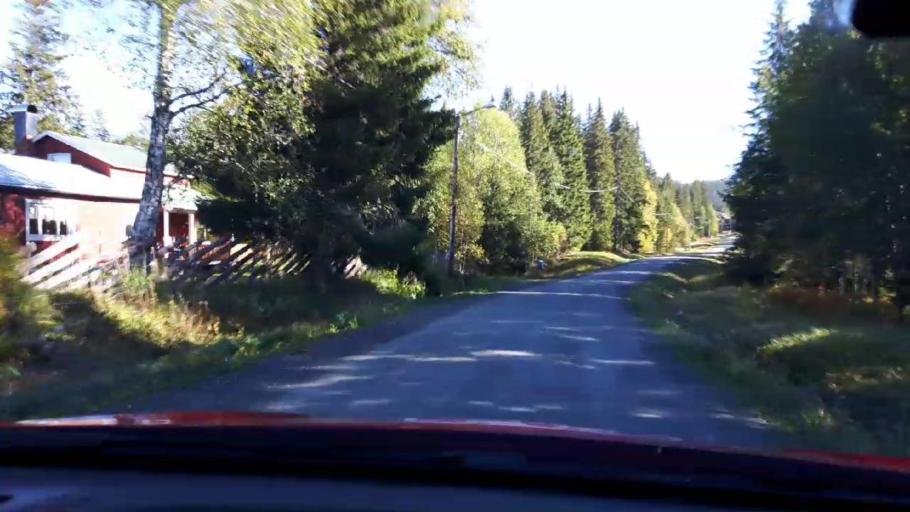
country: NO
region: Nord-Trondelag
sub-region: Lierne
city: Sandvika
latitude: 64.6462
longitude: 13.7383
